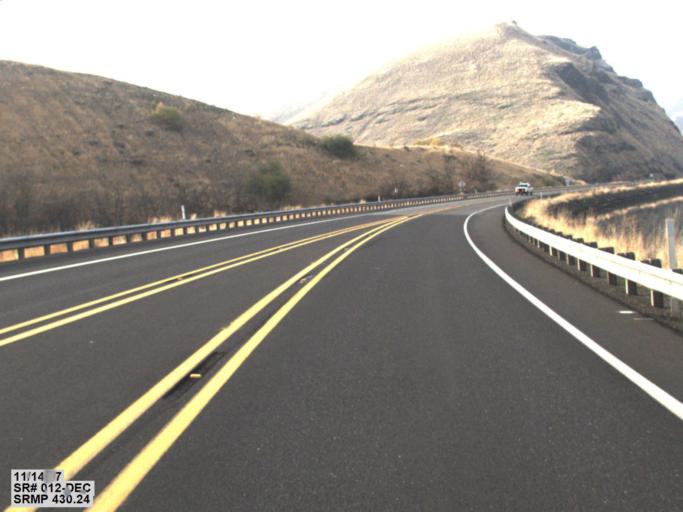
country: US
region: Washington
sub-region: Asotin County
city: Clarkston Heights-Vineland
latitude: 46.4198
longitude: -117.1150
